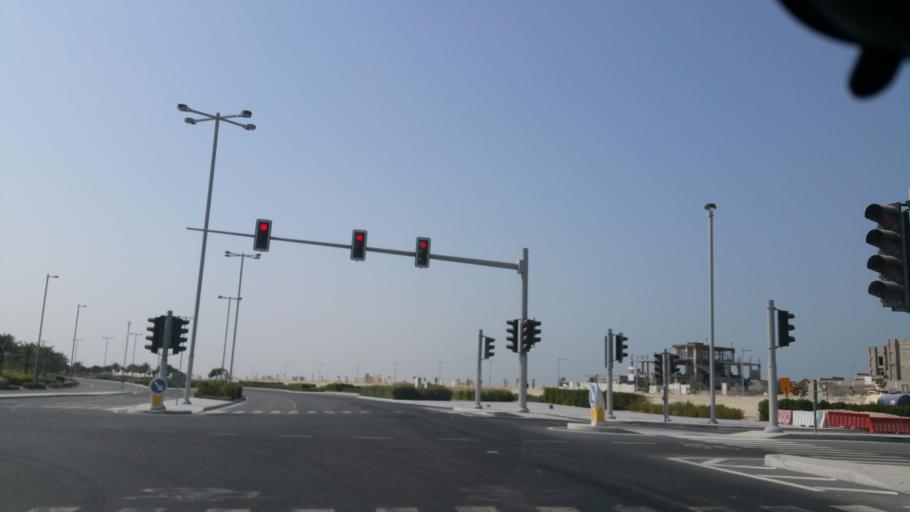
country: QA
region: Baladiyat Umm Salal
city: Umm Salal Muhammad
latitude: 25.4375
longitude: 51.5148
